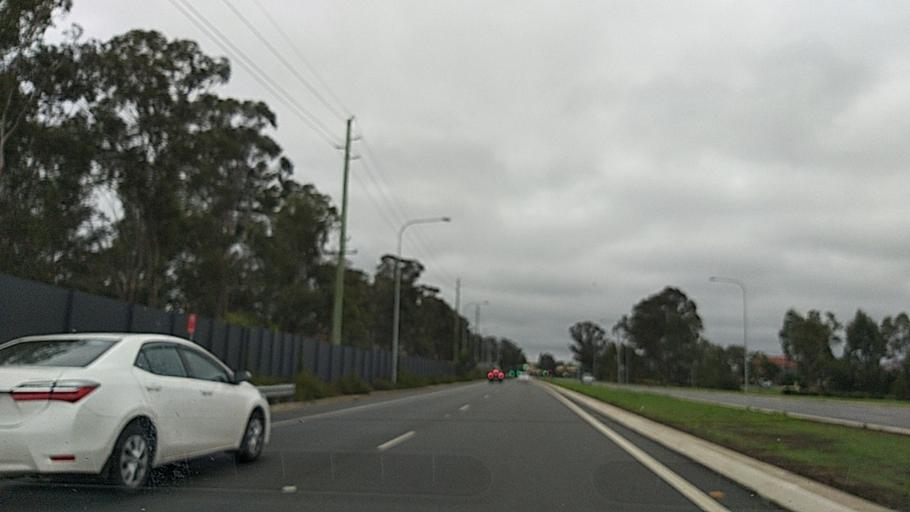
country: AU
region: New South Wales
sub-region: Penrith Municipality
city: Werrington Downs
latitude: -33.7253
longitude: 150.7212
